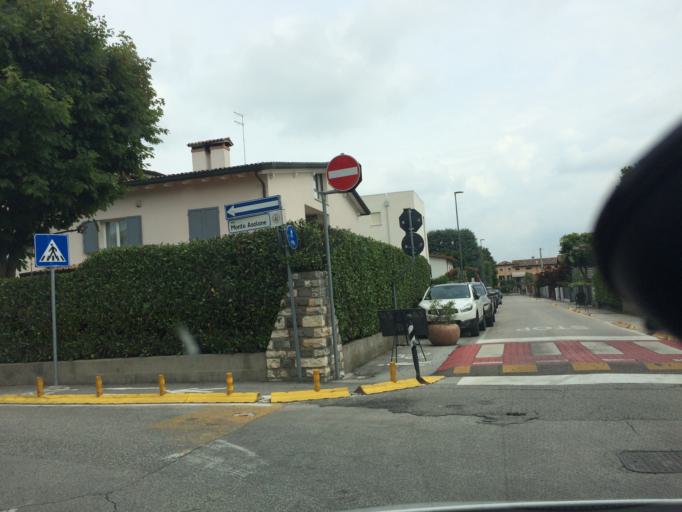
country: IT
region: Veneto
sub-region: Provincia di Padova
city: Cittadella
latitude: 45.6529
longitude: 11.7843
